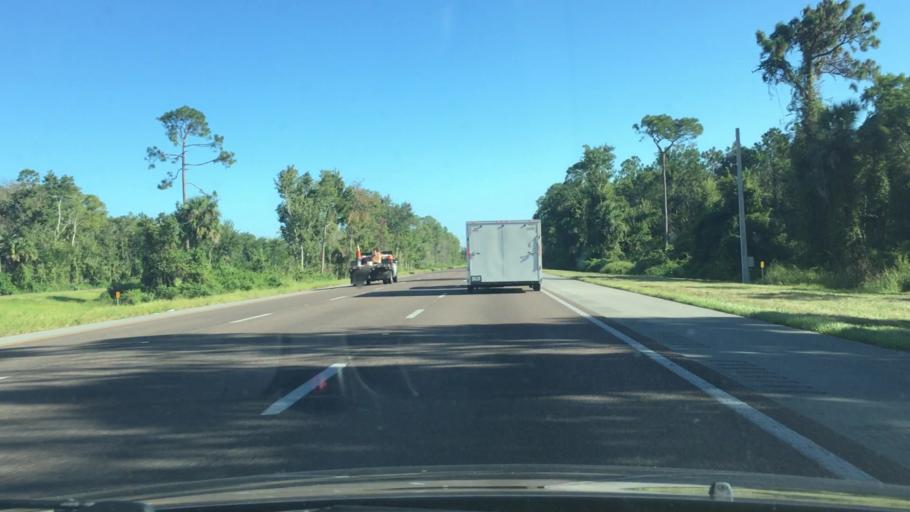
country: US
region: Florida
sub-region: Volusia County
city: Glencoe
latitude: 28.9736
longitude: -80.9627
